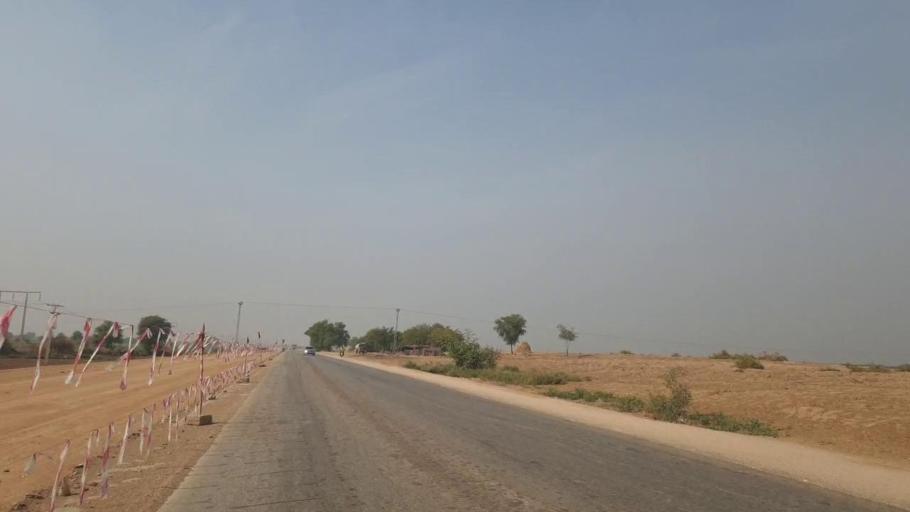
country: PK
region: Sindh
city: Sann
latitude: 26.1332
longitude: 68.0465
